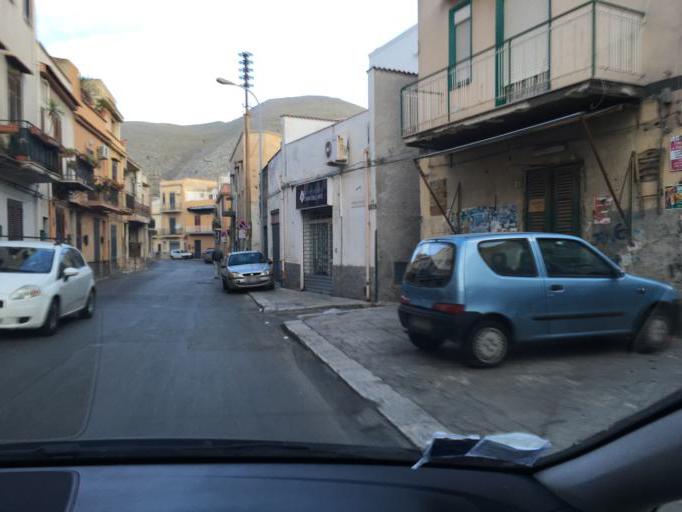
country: IT
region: Sicily
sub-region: Palermo
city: Isola delle Femmine
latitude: 38.1963
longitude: 13.3108
